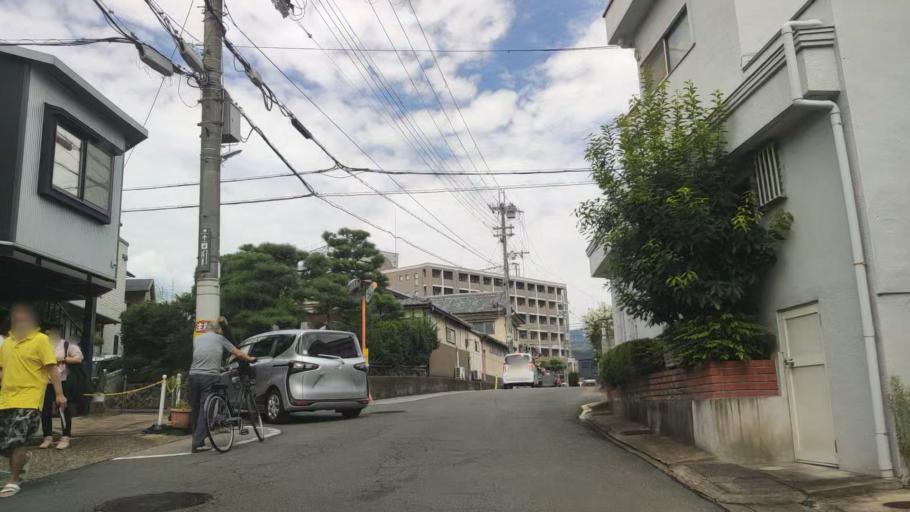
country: JP
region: Kyoto
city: Muko
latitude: 35.0162
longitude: 135.7026
